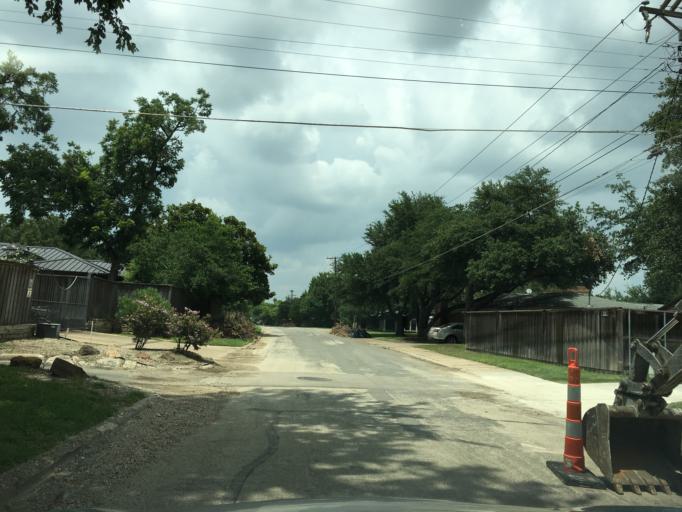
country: US
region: Texas
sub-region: Dallas County
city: University Park
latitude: 32.8979
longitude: -96.7838
